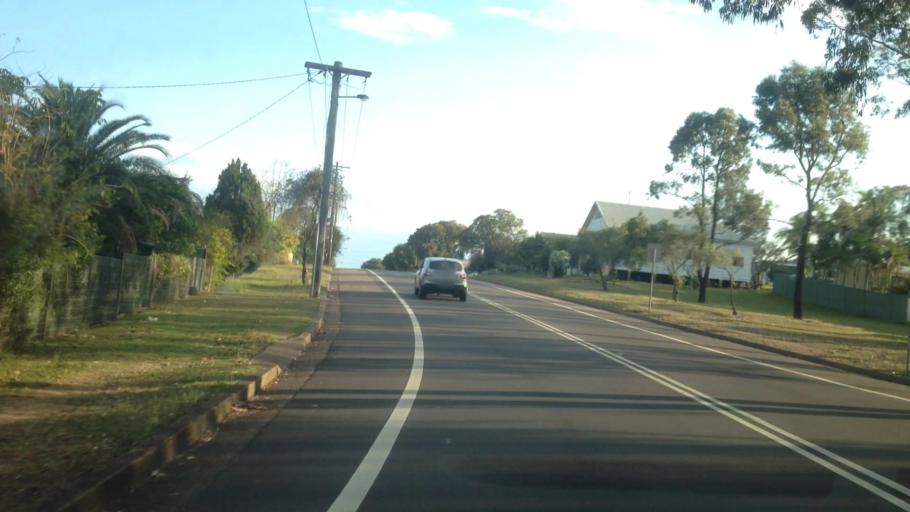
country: AU
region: New South Wales
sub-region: Cessnock
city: Kurri Kurri
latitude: -32.8272
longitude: 151.4818
